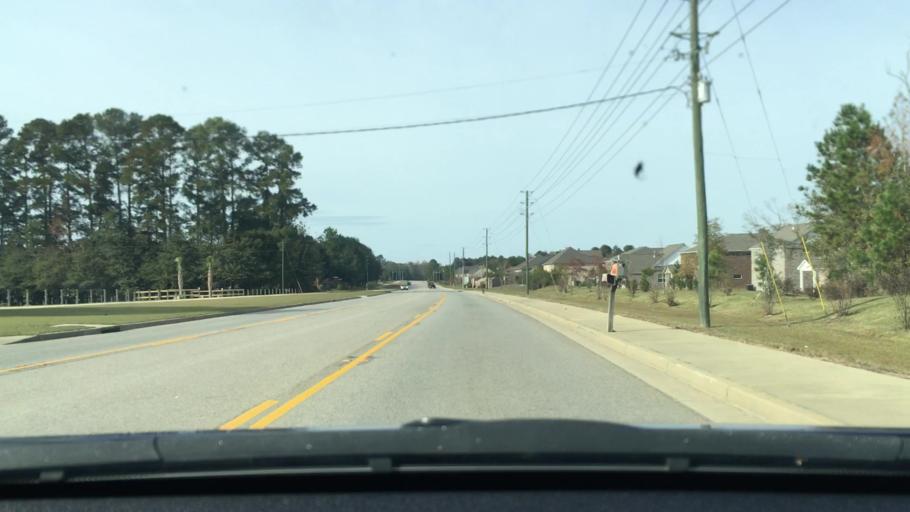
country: US
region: South Carolina
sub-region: Sumter County
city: Cane Savannah
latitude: 33.9291
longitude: -80.4104
